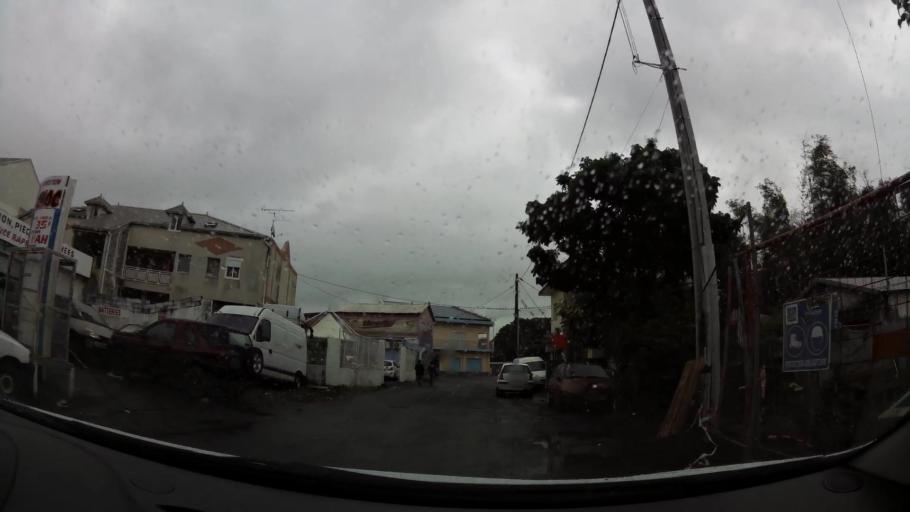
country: RE
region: Reunion
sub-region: Reunion
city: Saint-Andre
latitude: -20.9577
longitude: 55.6509
